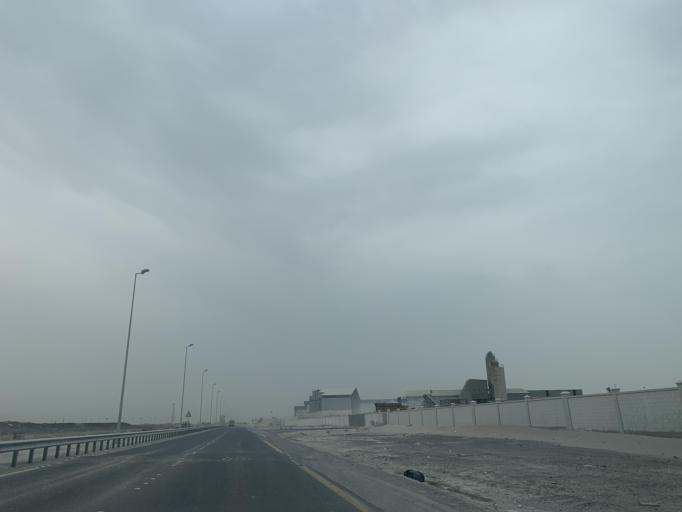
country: BH
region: Muharraq
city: Al Hadd
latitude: 26.2060
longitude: 50.6670
